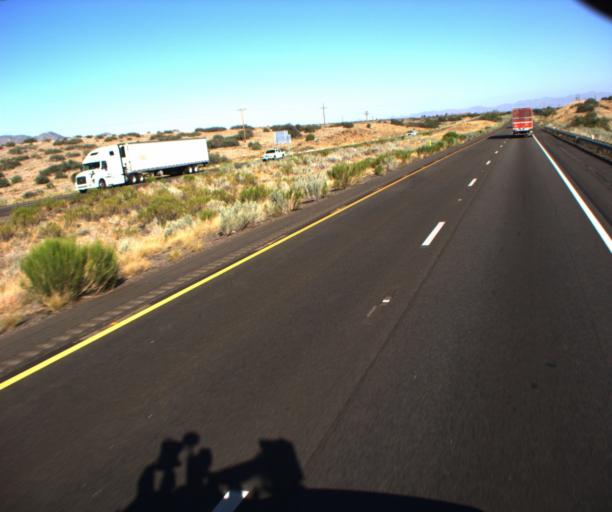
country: US
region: Arizona
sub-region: Mohave County
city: New Kingman-Butler
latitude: 35.1875
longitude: -113.8139
